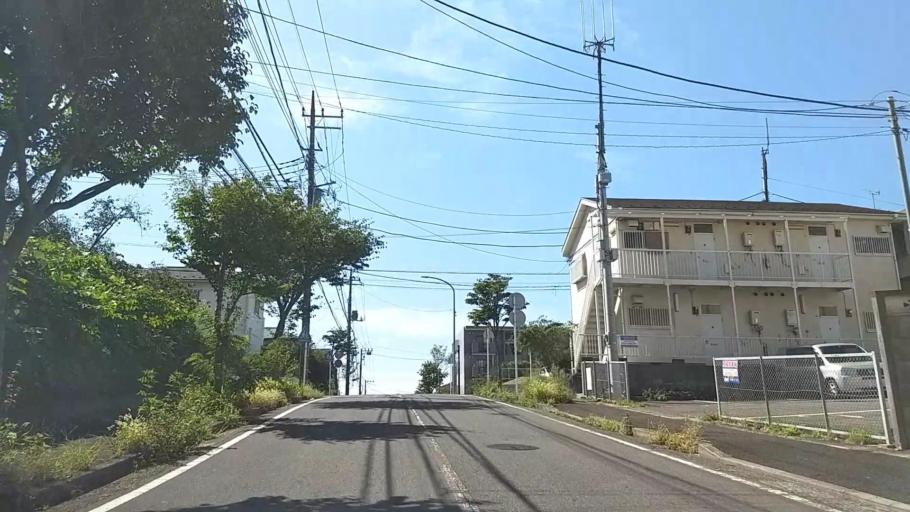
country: JP
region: Tokyo
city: Chofugaoka
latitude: 35.5699
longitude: 139.5378
